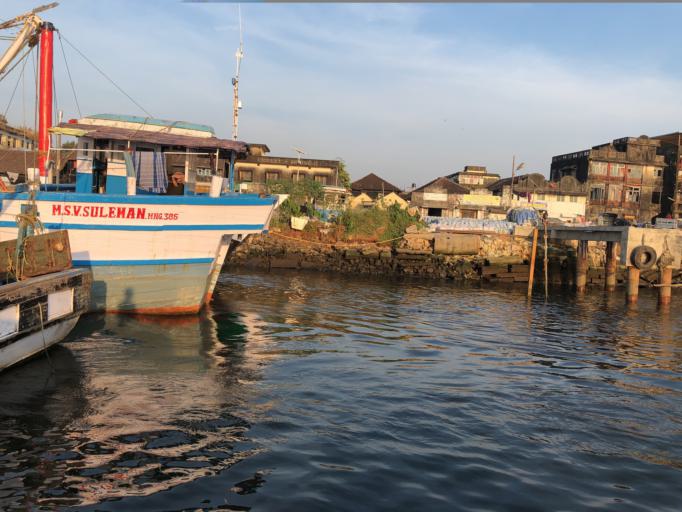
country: IN
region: Karnataka
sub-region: Dakshina Kannada
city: Mangalore
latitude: 12.8645
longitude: 74.8306
